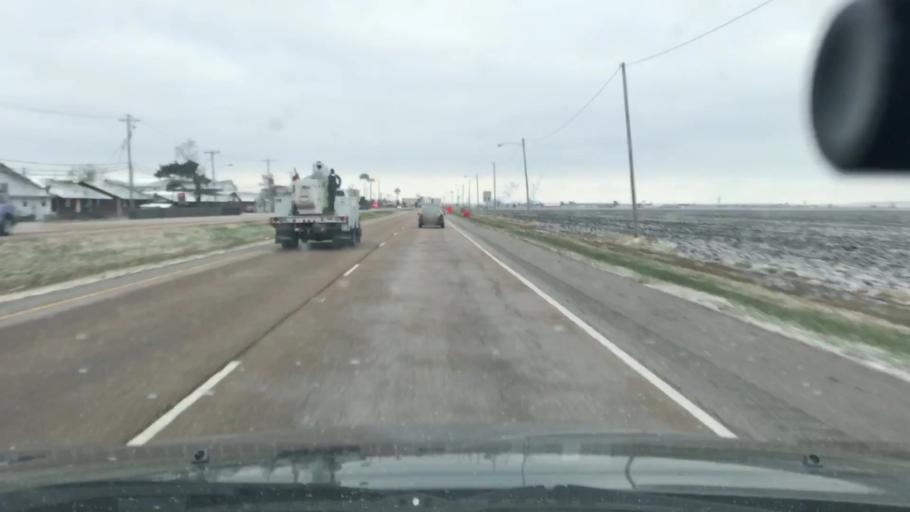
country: US
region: Illinois
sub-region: Madison County
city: Pontoon Beach
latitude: 38.7401
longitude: -90.0710
